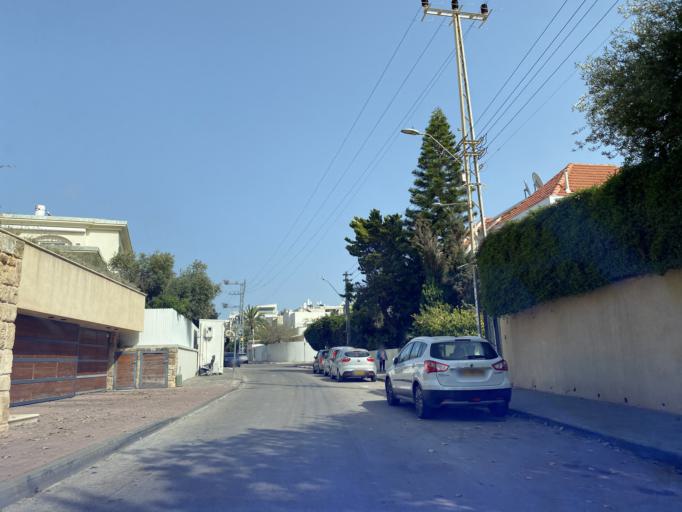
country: IL
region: Tel Aviv
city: Herzliya Pituah
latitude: 32.1743
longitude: 34.8063
